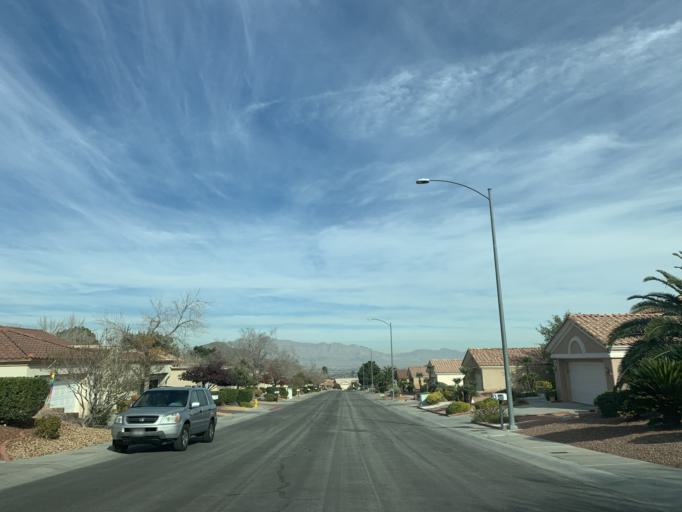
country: US
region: Nevada
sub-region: Clark County
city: Summerlin South
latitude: 36.2150
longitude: -115.3302
